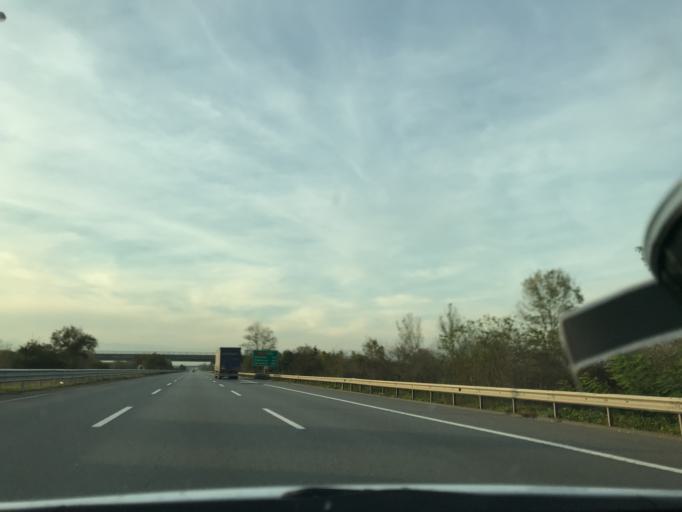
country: TR
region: Duzce
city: Cilimli
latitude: 40.8358
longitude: 31.0340
